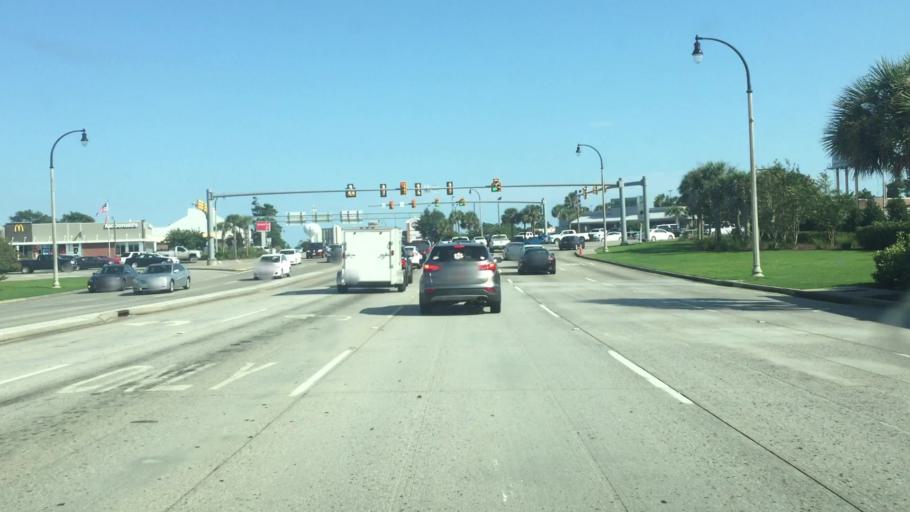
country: US
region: South Carolina
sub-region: Horry County
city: North Myrtle Beach
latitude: 33.8291
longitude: -78.6807
